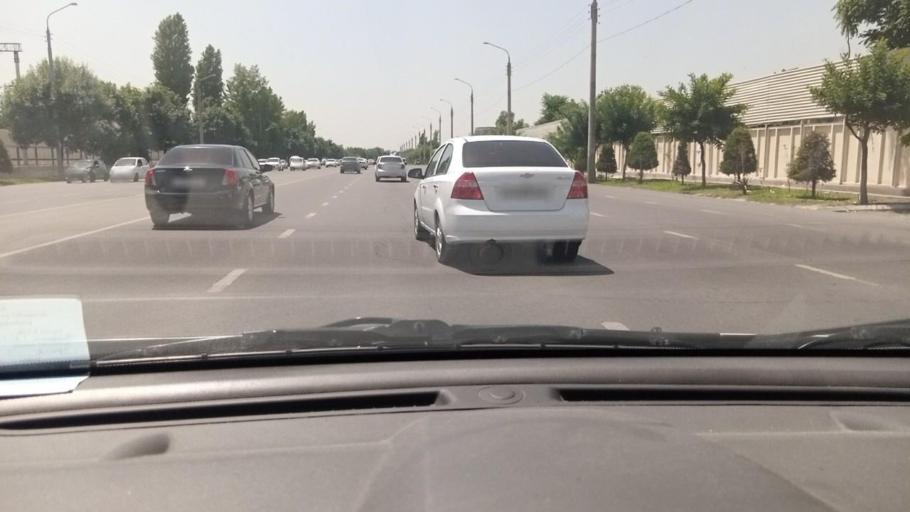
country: UZ
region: Toshkent Shahri
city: Tashkent
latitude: 41.2763
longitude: 69.2711
